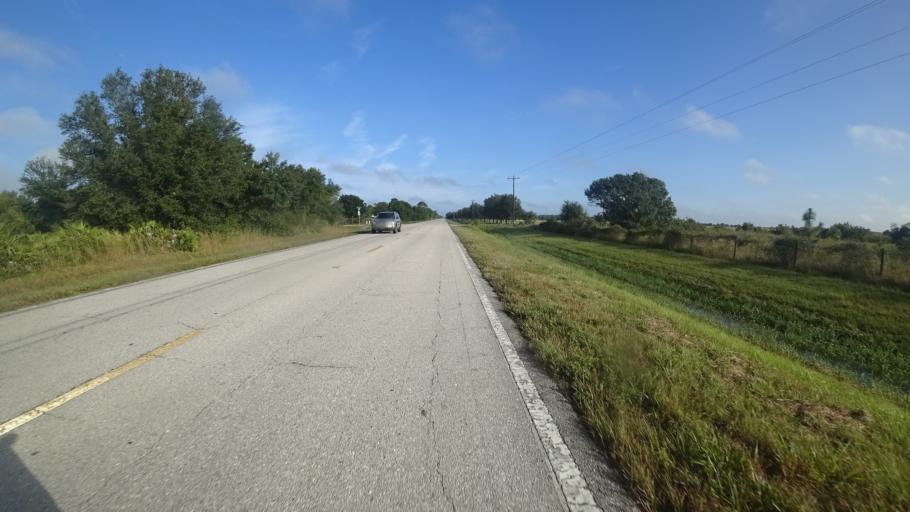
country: US
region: Florida
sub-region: Sarasota County
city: The Meadows
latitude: 27.4158
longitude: -82.3037
